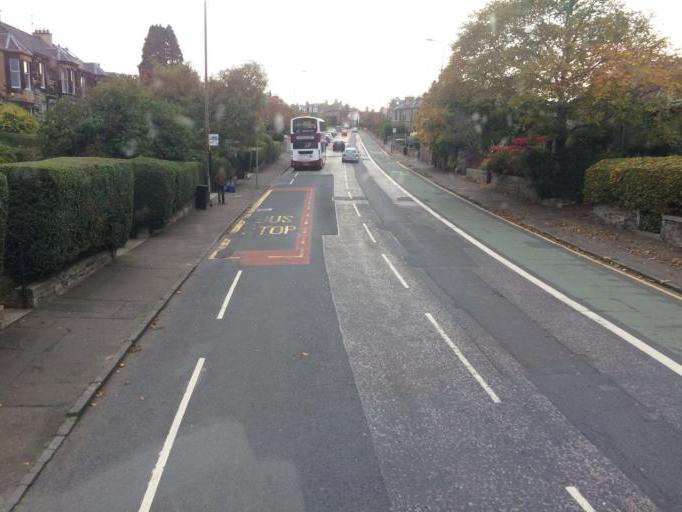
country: GB
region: Scotland
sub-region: Midlothian
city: Loanhead
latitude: 55.9189
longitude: -3.1673
